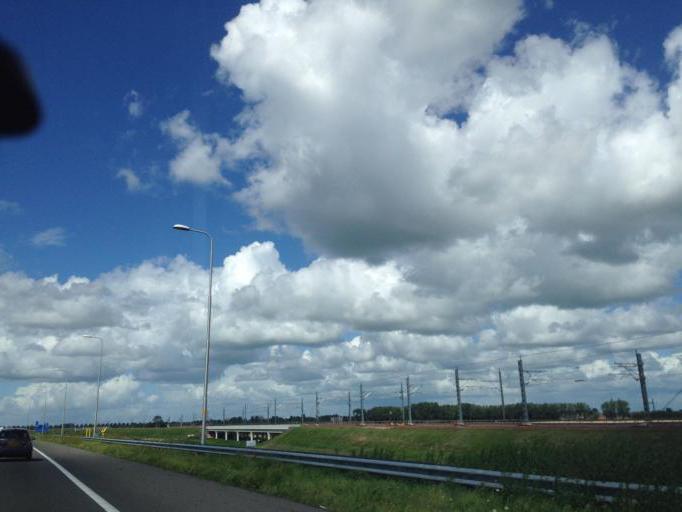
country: NL
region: Overijssel
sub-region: Gemeente Kampen
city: Kampen
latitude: 52.5236
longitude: 5.9235
